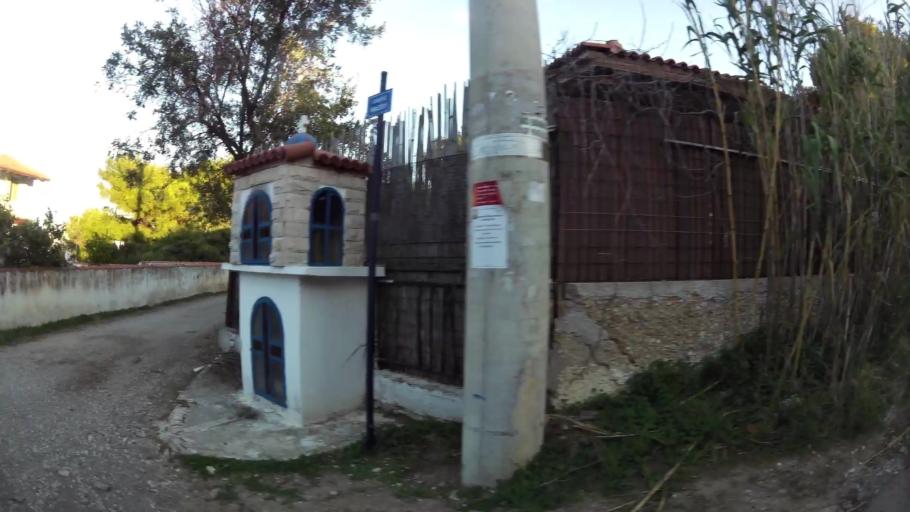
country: GR
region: Attica
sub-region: Nomarchia Anatolikis Attikis
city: Rafina
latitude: 38.0083
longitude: 24.0096
